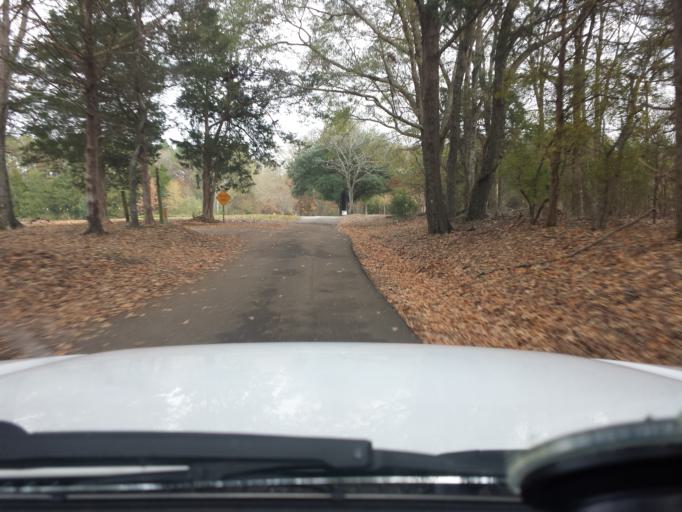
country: US
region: Mississippi
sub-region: Yazoo County
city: Yazoo City
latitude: 32.7852
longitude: -90.1883
